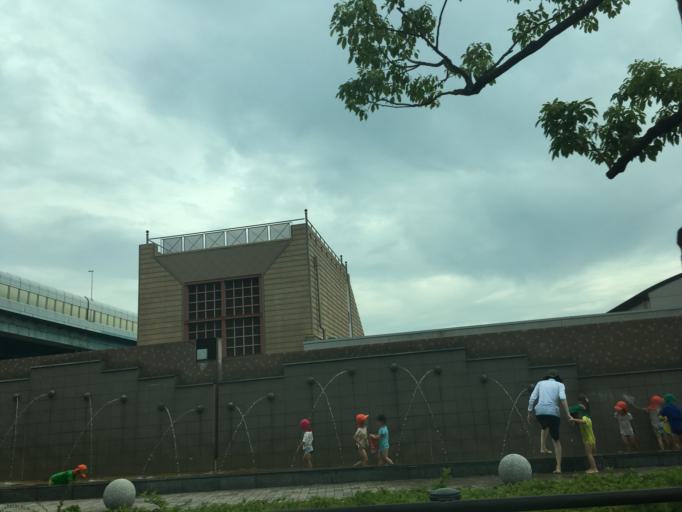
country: JP
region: Hyogo
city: Ashiya
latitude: 34.7125
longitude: 135.3096
